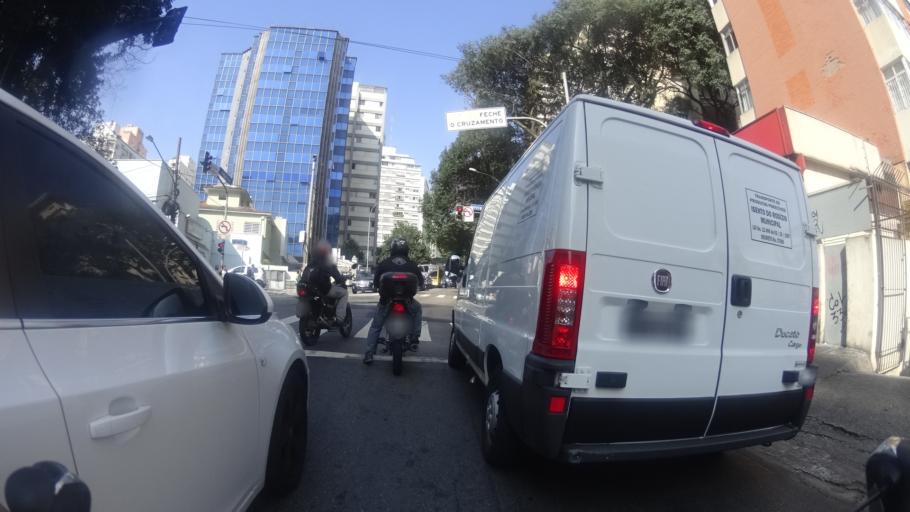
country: BR
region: Sao Paulo
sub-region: Sao Paulo
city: Sao Paulo
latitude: -23.5413
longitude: -46.6564
